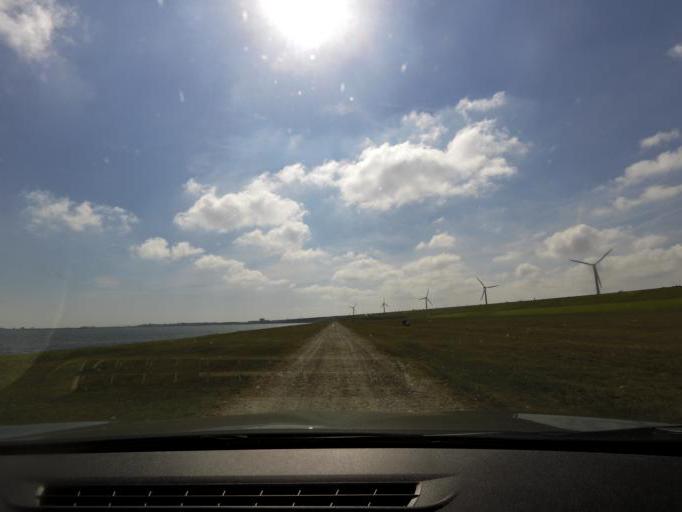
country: NL
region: South Holland
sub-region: Gemeente Hellevoetsluis
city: Nieuw-Helvoet
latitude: 51.8418
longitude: 4.0689
